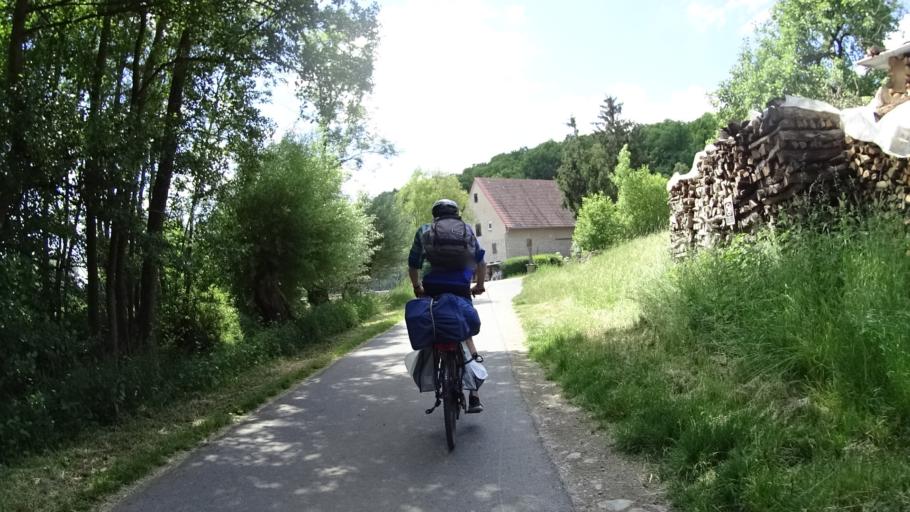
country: DE
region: Bavaria
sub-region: Regierungsbezirk Unterfranken
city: Bieberehren
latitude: 49.5164
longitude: 10.0030
